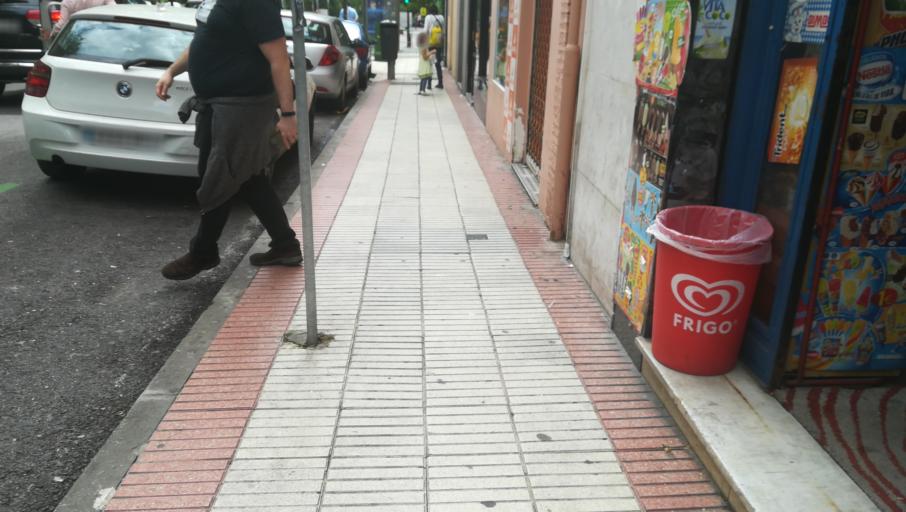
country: ES
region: Madrid
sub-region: Provincia de Madrid
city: Retiro
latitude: 40.4165
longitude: -3.6702
